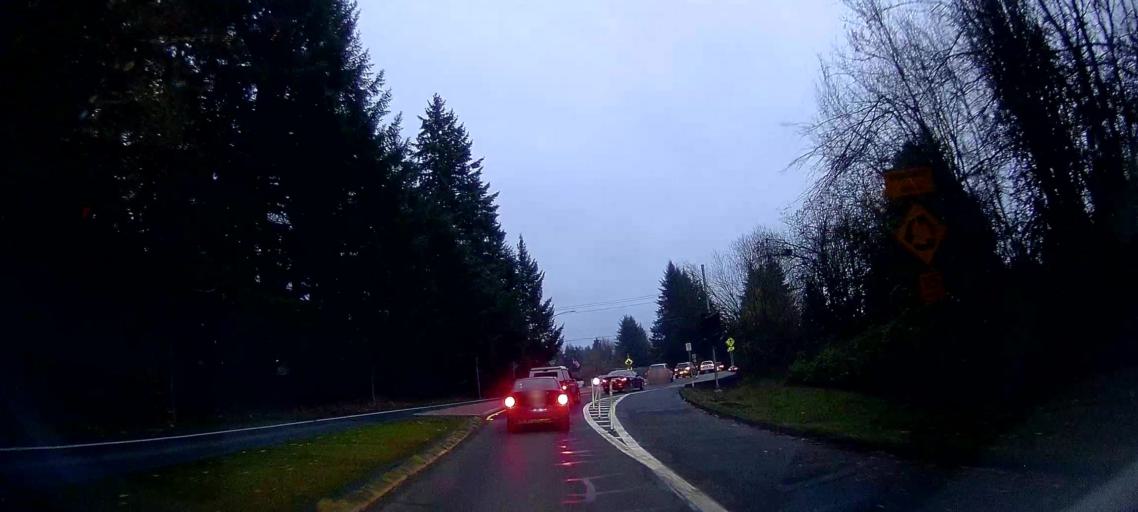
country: US
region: Washington
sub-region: Thurston County
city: Olympia
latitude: 47.0240
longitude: -122.8786
